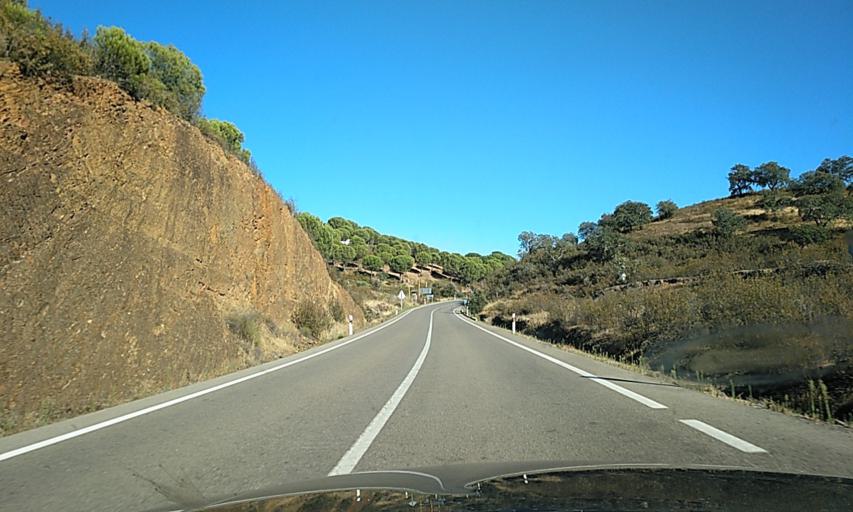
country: ES
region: Andalusia
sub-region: Provincia de Huelva
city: Santa Barbara de Casa
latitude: 37.8040
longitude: -7.2012
